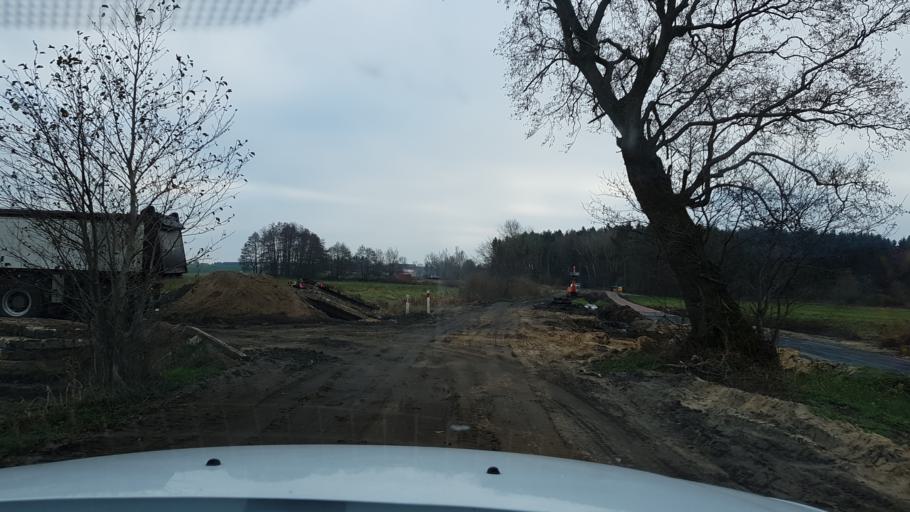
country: PL
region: West Pomeranian Voivodeship
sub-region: Powiat kolobrzeski
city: Grzybowo
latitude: 54.1268
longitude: 15.5167
